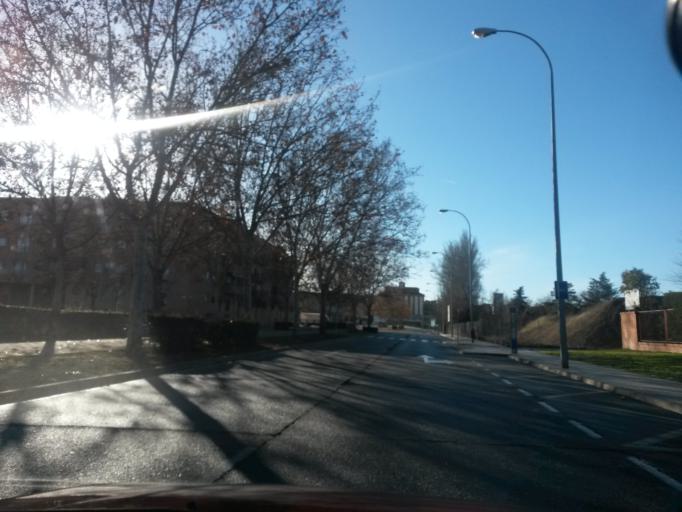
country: ES
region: Castille and Leon
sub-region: Provincia de Salamanca
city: Salamanca
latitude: 40.9575
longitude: -5.6860
